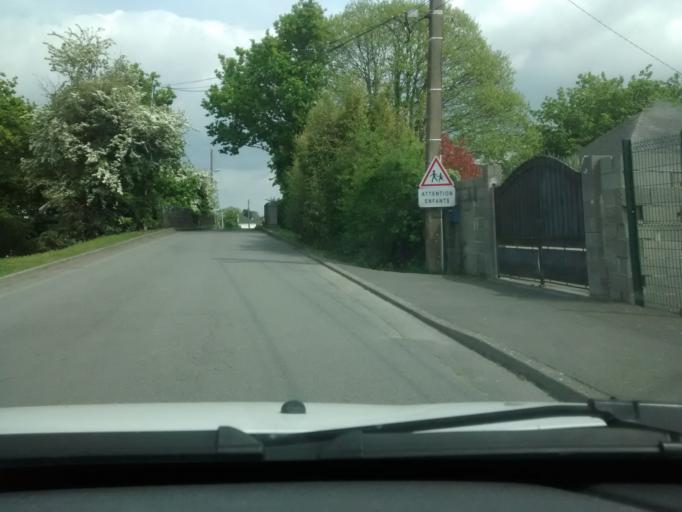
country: FR
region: Brittany
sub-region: Departement d'Ille-et-Vilaine
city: Dinard
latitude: 48.6175
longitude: -2.0645
